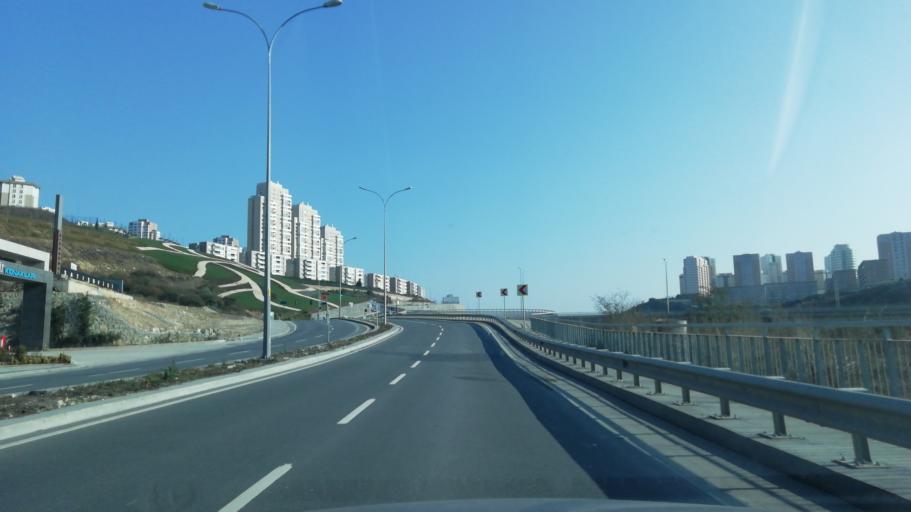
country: TR
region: Istanbul
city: Esenyurt
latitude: 41.0811
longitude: 28.6840
